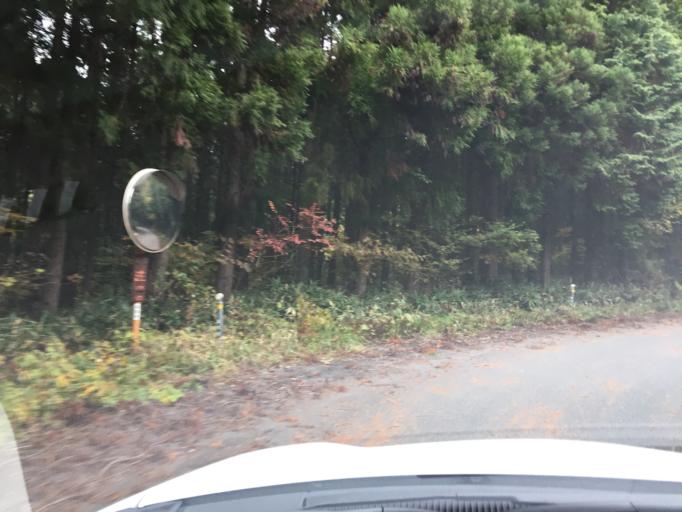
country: JP
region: Fukushima
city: Iwaki
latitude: 37.0980
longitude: 140.7832
